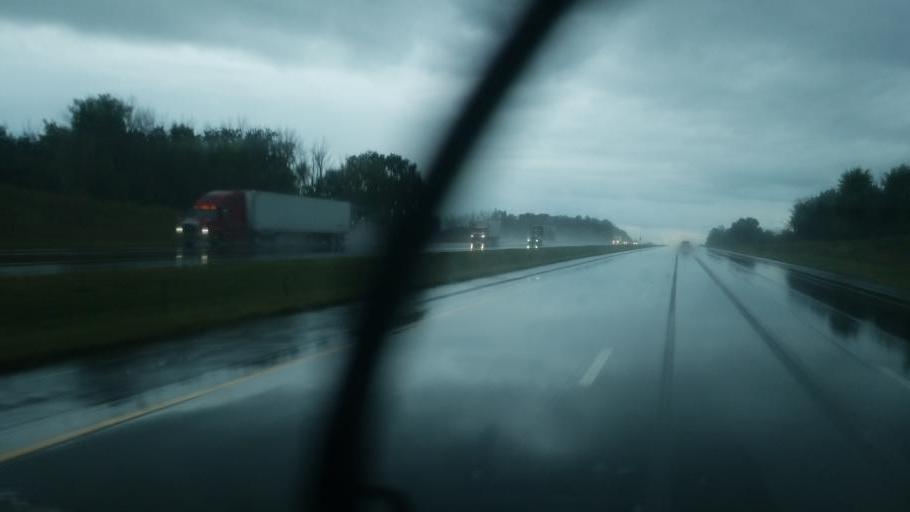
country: US
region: Ohio
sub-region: Medina County
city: Medina
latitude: 41.0910
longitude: -81.8294
